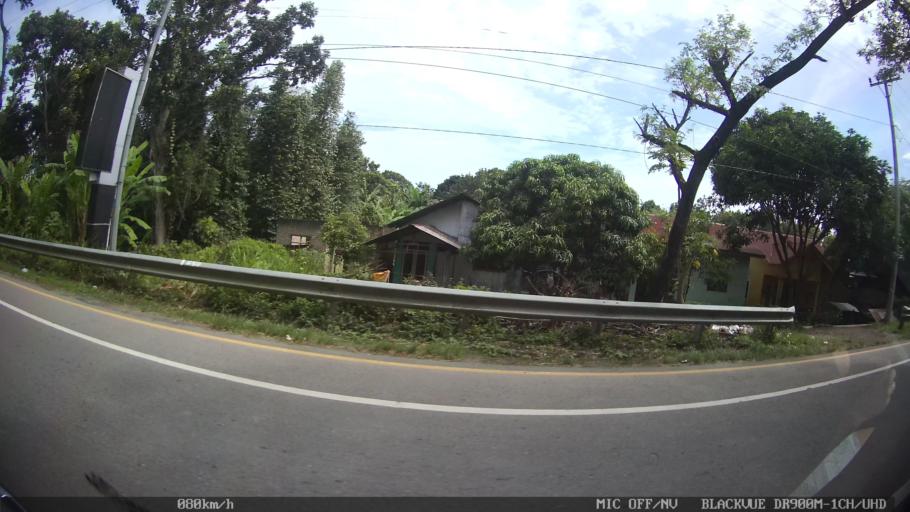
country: ID
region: North Sumatra
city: Percut
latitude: 3.5991
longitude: 98.8310
